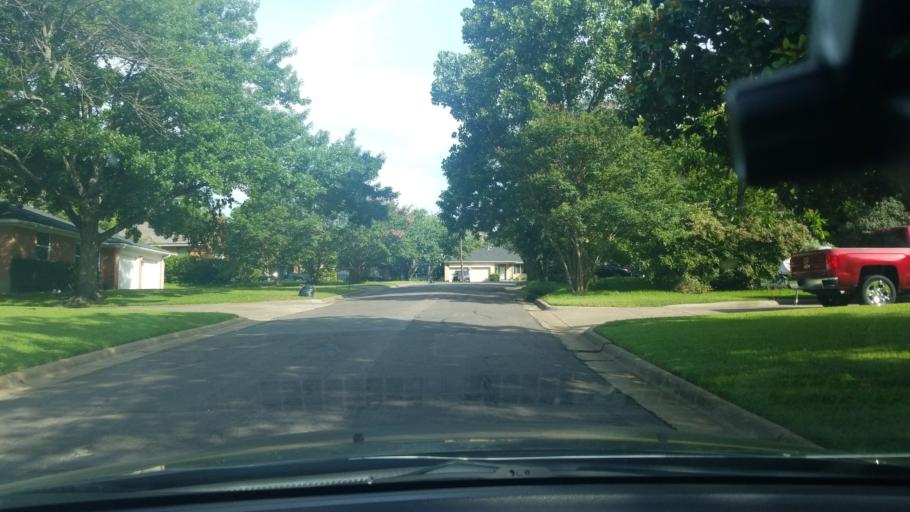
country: US
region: Texas
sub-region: Dallas County
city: Highland Park
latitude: 32.8002
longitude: -96.7104
